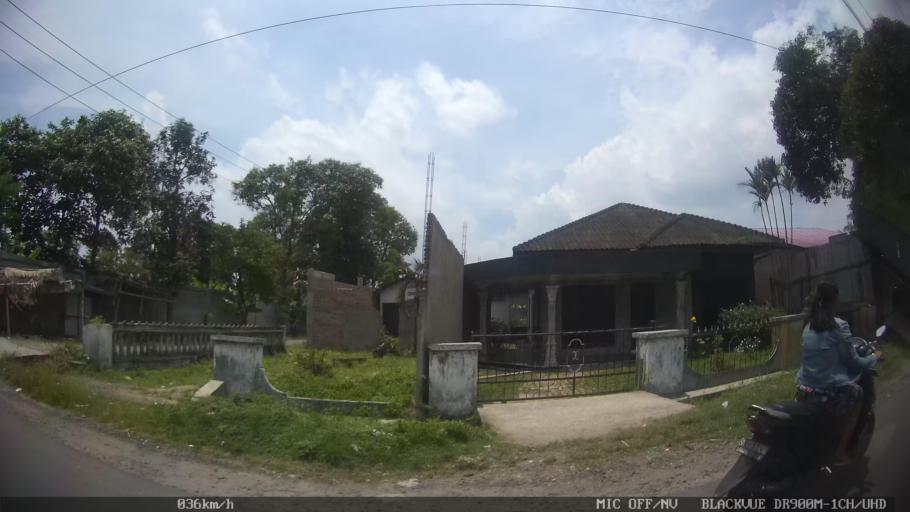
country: ID
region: North Sumatra
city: Labuhan Deli
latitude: 3.7090
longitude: 98.6746
